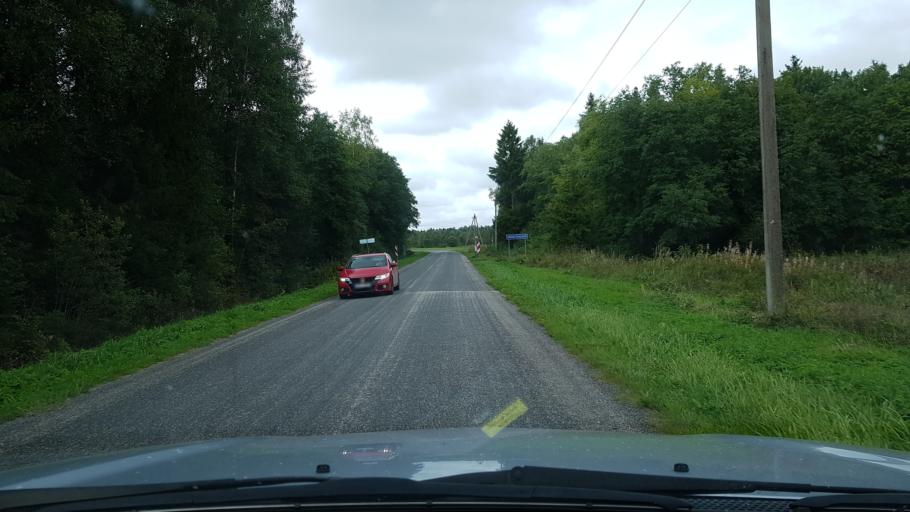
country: EE
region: Harju
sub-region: Rae vald
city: Vaida
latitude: 59.3109
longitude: 24.9653
